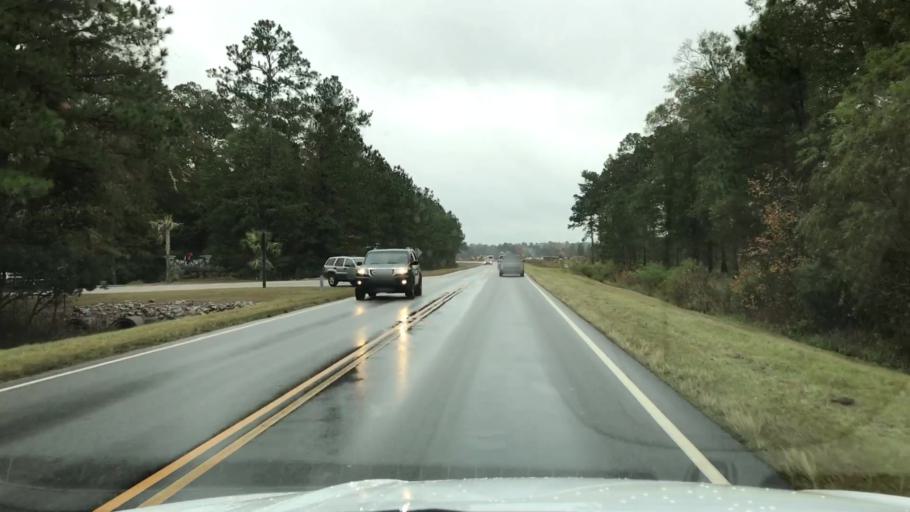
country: US
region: South Carolina
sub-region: Horry County
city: Myrtle Beach
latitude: 33.7585
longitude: -78.8841
